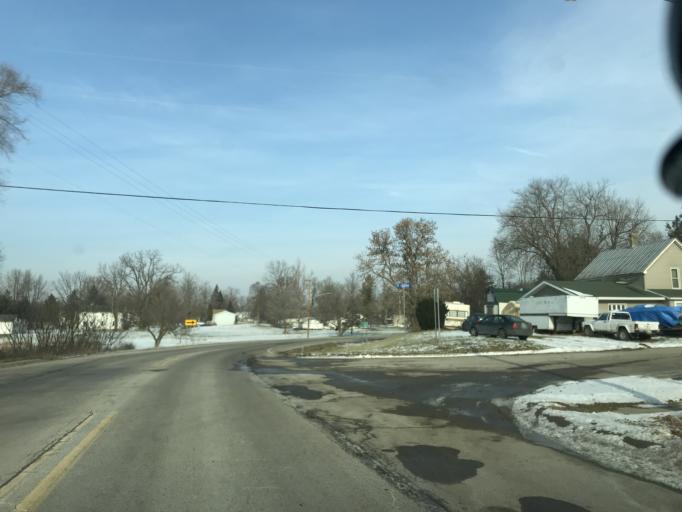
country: US
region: Michigan
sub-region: Barry County
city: Nashville
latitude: 42.5960
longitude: -85.0946
